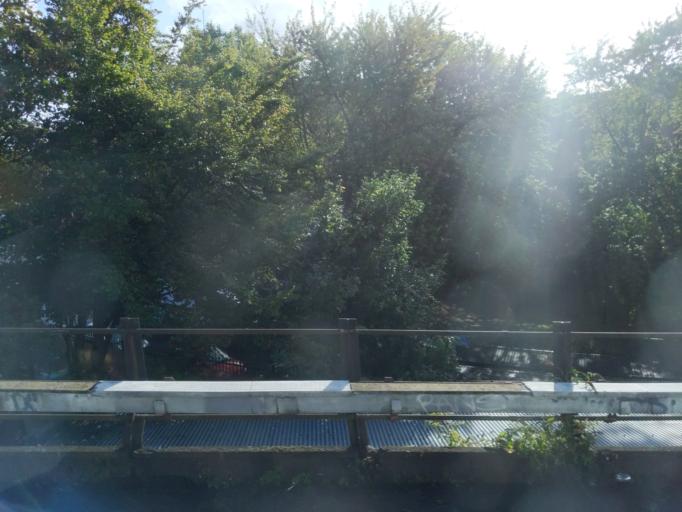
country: GB
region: England
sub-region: Greater London
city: Poplar
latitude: 51.4796
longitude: -0.0285
